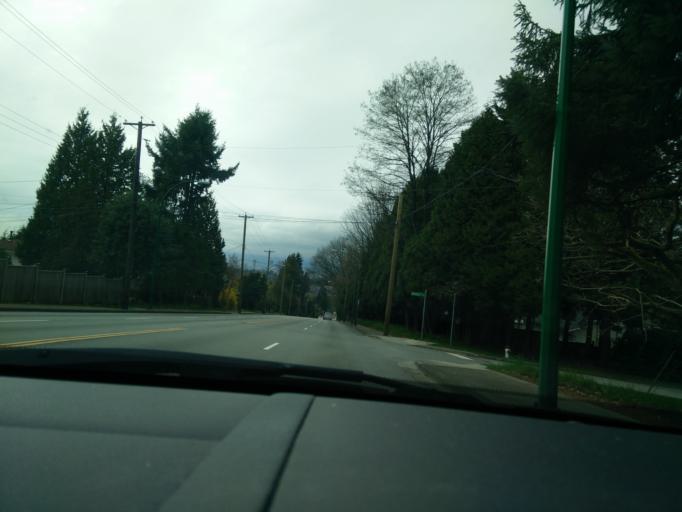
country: CA
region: British Columbia
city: Burnaby
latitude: 49.2306
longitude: -122.9488
